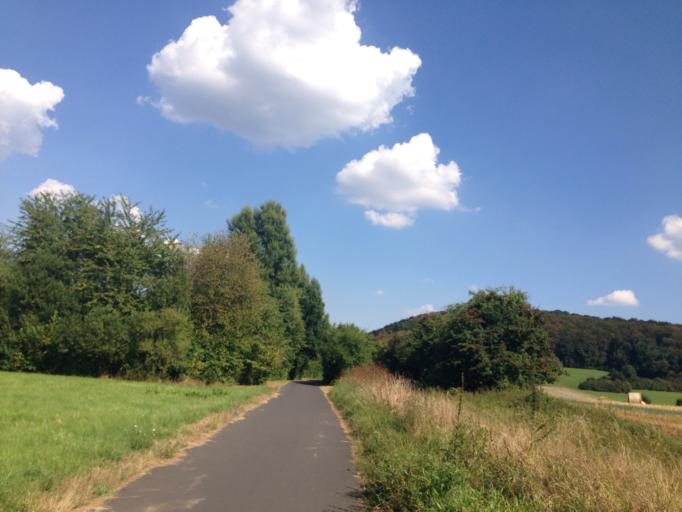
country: DE
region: Hesse
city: Beuern
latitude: 50.6700
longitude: 8.8053
